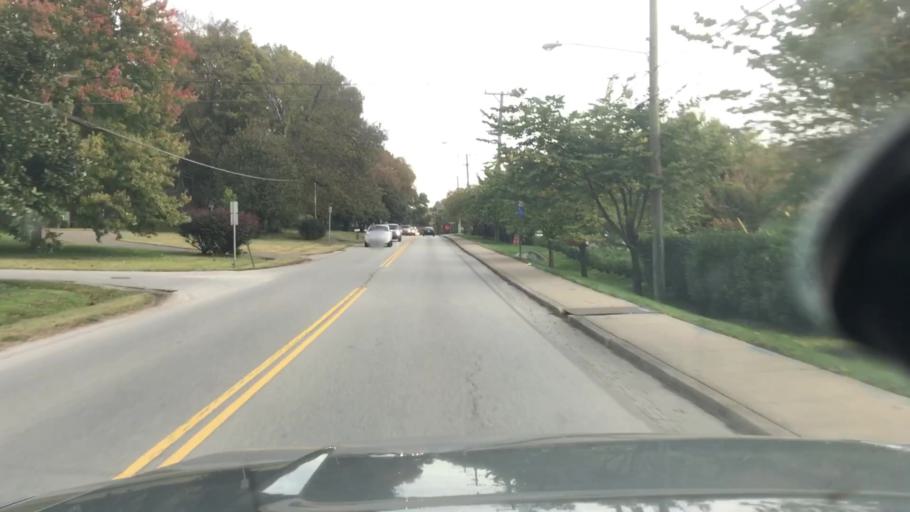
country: US
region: Tennessee
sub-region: Davidson County
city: Oak Hill
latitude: 36.1041
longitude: -86.8015
